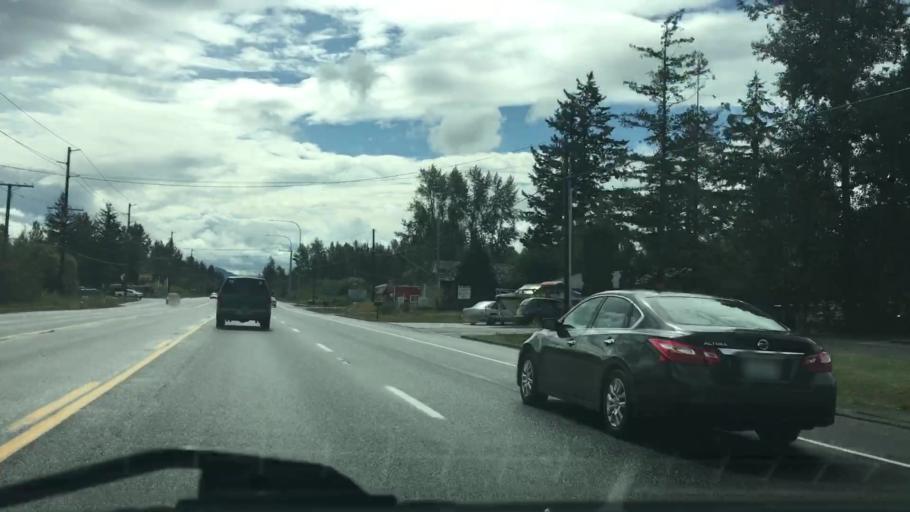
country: US
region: Washington
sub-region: Whatcom County
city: Bellingham
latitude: 48.8205
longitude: -122.4843
